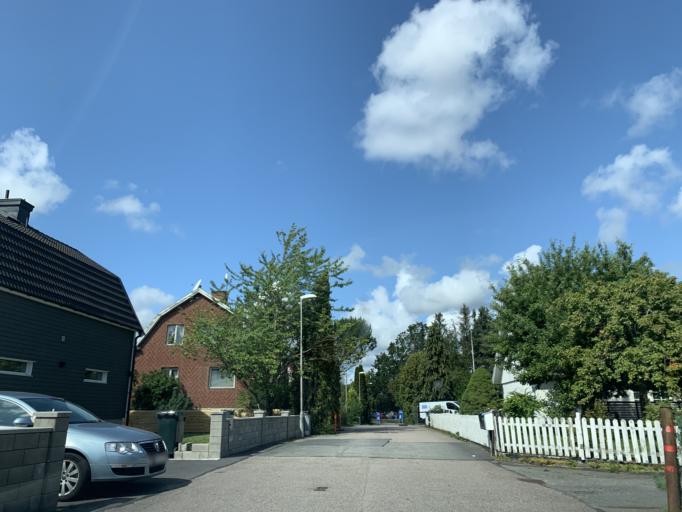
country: SE
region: Vaestra Goetaland
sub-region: Goteborg
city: Eriksbo
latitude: 57.7685
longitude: 12.0293
